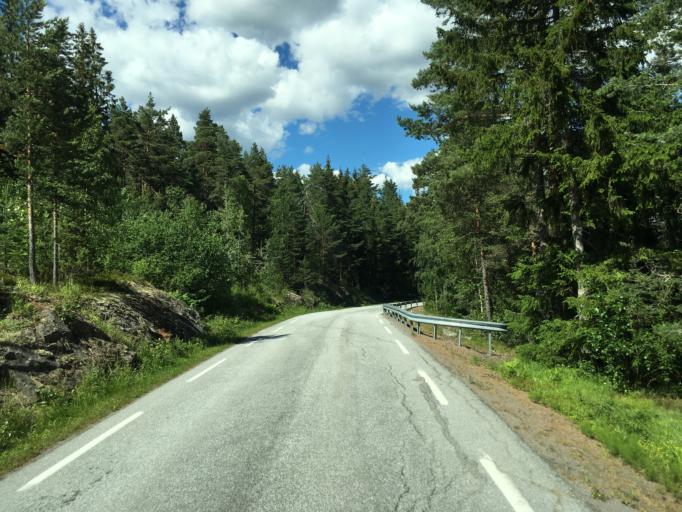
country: NO
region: Oppland
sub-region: Jevnaker
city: Jevnaker
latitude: 60.3496
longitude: 10.3609
